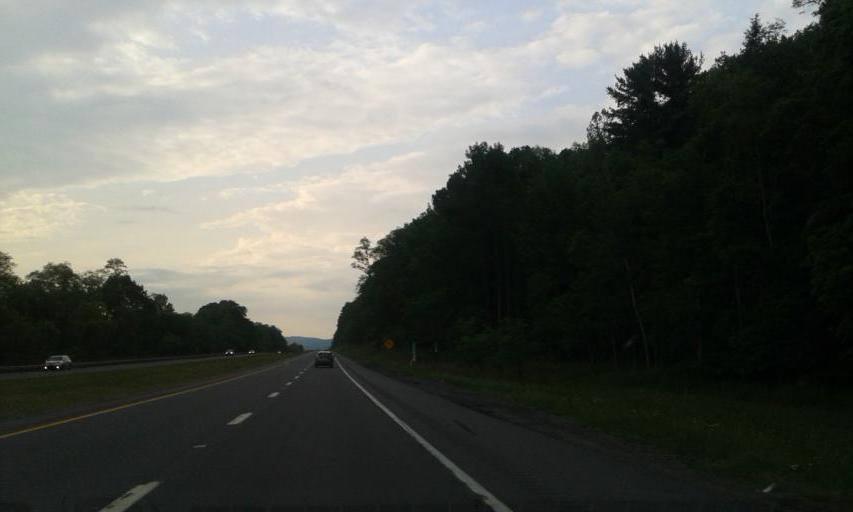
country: US
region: Pennsylvania
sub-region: Susquehanna County
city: Hallstead
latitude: 41.9383
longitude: -75.7329
